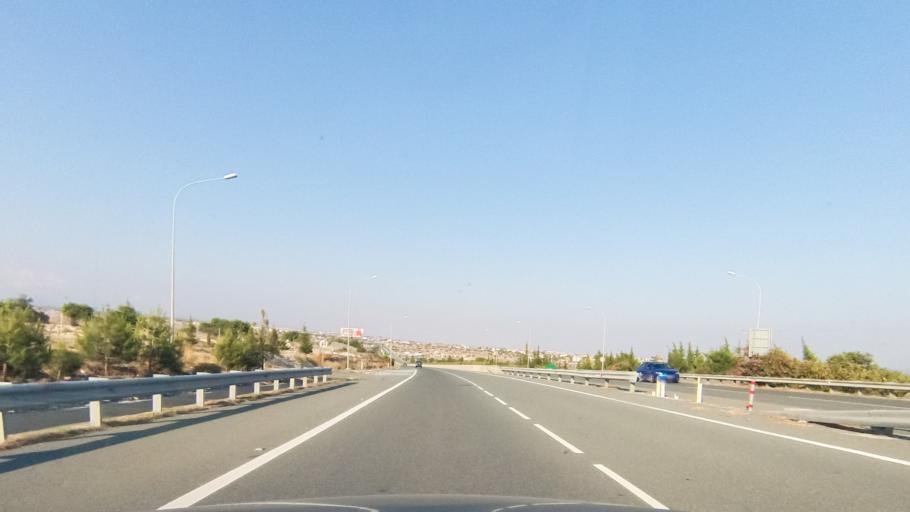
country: CY
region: Limassol
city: Erimi
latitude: 34.6816
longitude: 32.8963
